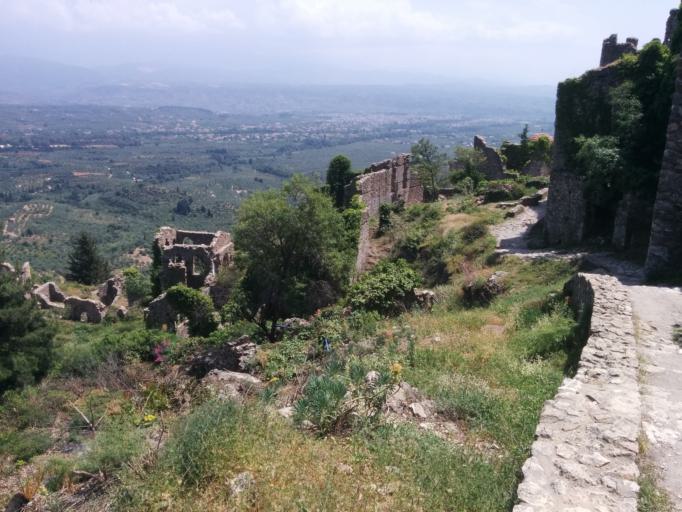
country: GR
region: Peloponnese
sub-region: Nomos Lakonias
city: Magoula
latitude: 37.0738
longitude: 22.3663
